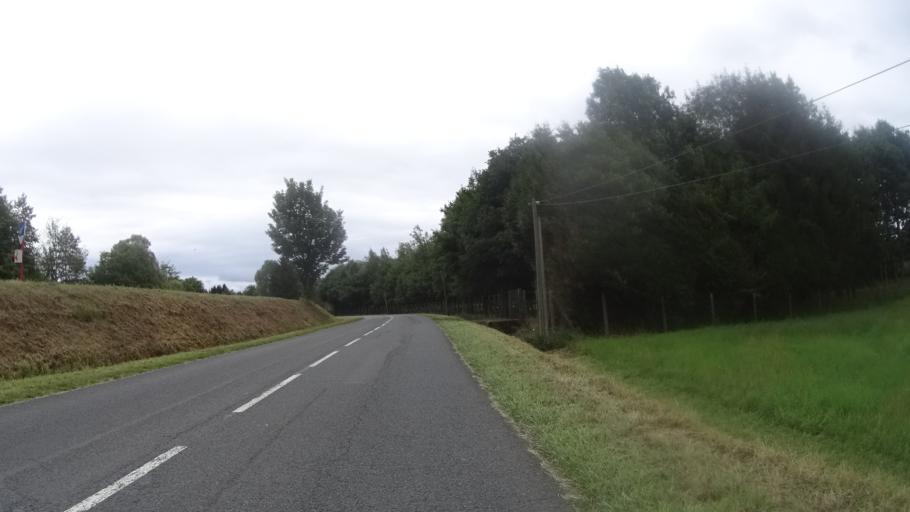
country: FR
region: Lorraine
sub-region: Departement de la Moselle
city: Dieuze
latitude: 48.6895
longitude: 6.6809
